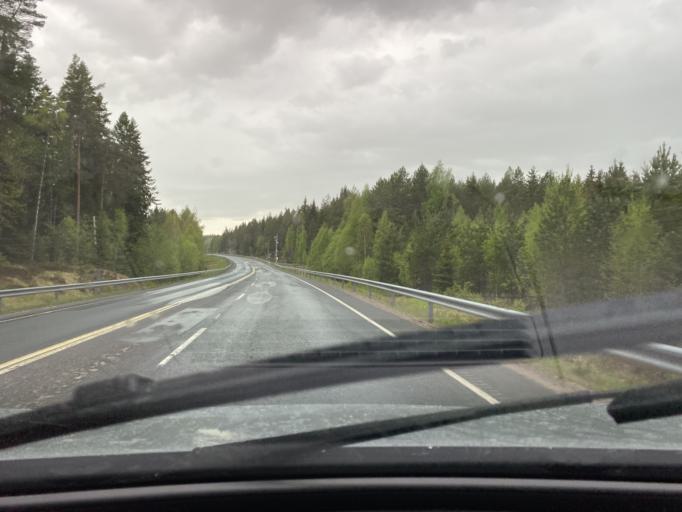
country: FI
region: Varsinais-Suomi
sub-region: Salo
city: Suomusjaervi
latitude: 60.3718
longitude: 23.6666
